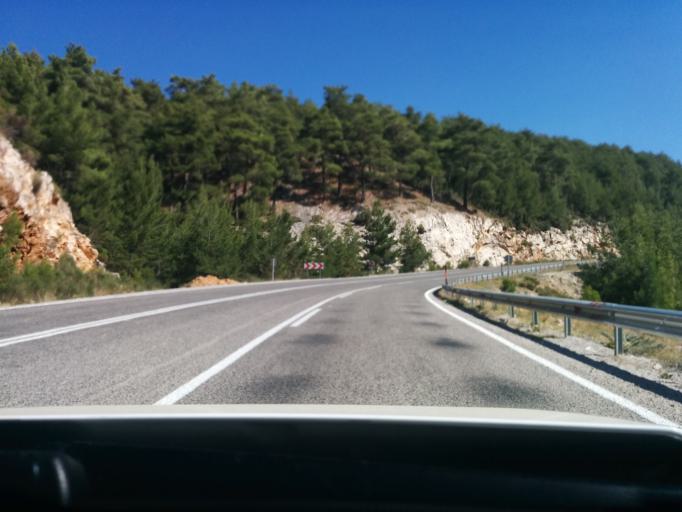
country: TR
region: Mugla
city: Kemer
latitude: 36.7858
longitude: 29.4746
